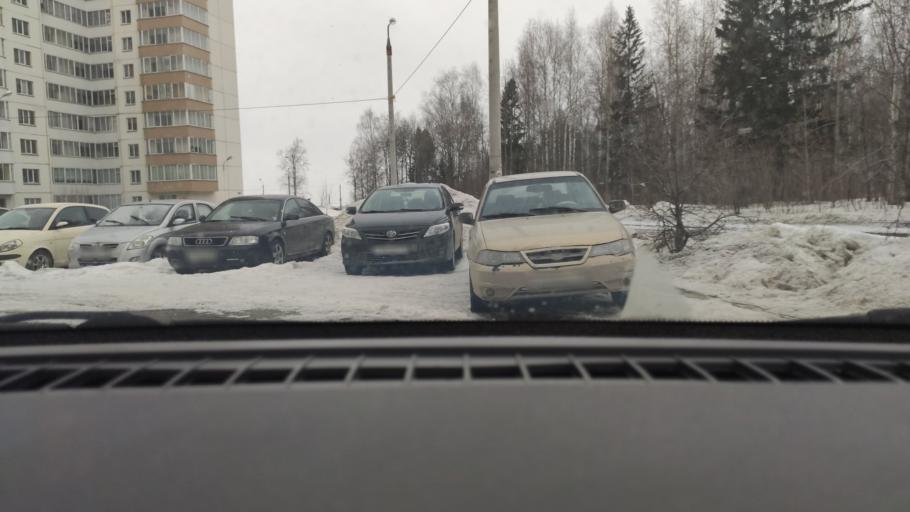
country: RU
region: Perm
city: Polazna
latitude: 58.1346
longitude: 56.4003
